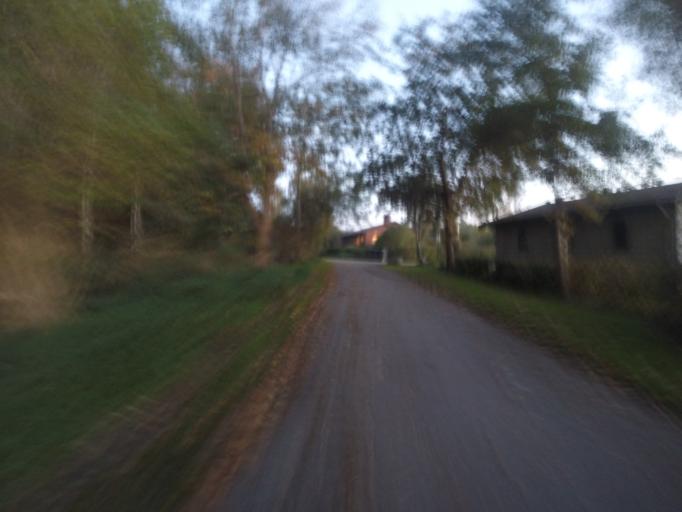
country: DK
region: Capital Region
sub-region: Vallensbaek Kommune
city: Vallensbaek
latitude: 55.6333
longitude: 12.3596
